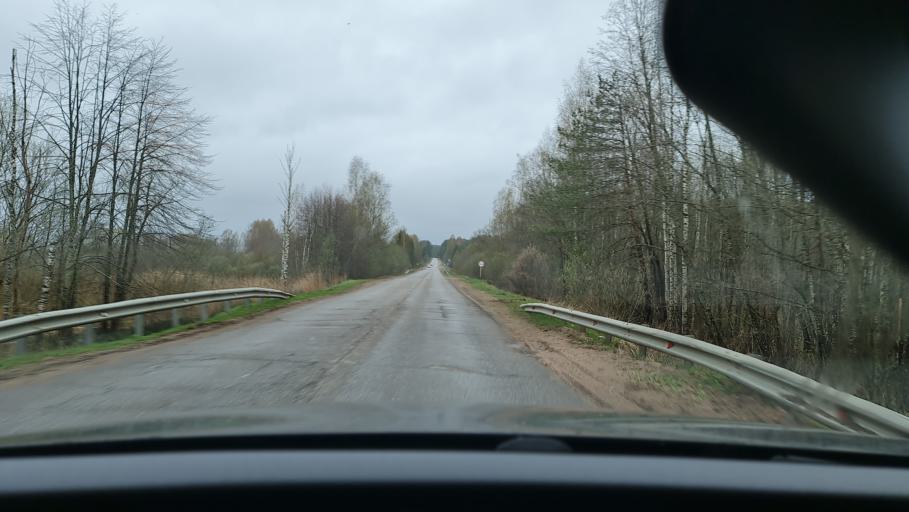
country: RU
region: Novgorod
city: Demyansk
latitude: 57.6592
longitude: 32.5060
